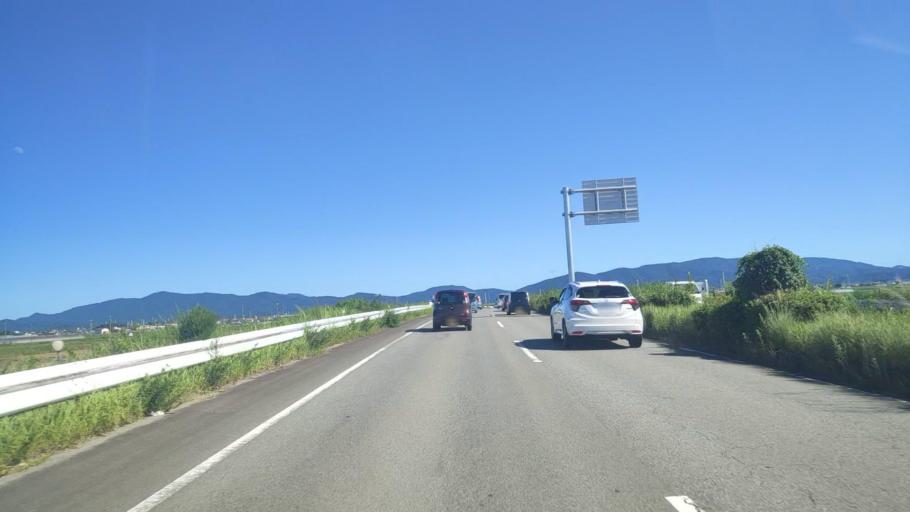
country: JP
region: Mie
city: Ise
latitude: 34.5309
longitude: 136.6823
